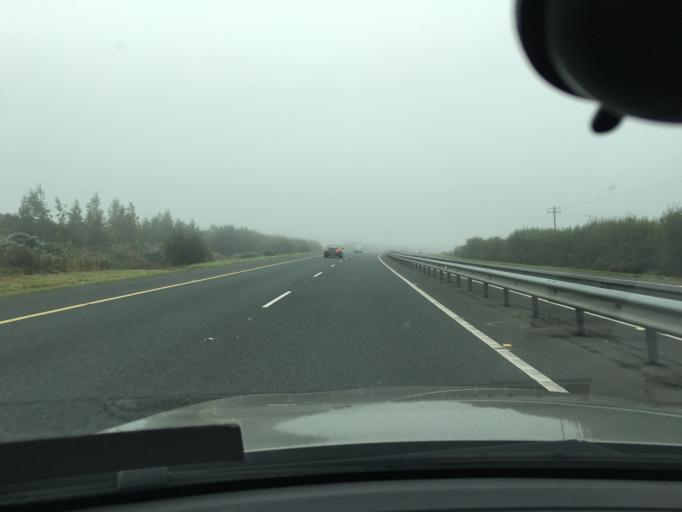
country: IE
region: Leinster
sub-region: An Iarmhi
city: Athlone
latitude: 53.3594
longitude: -8.0634
